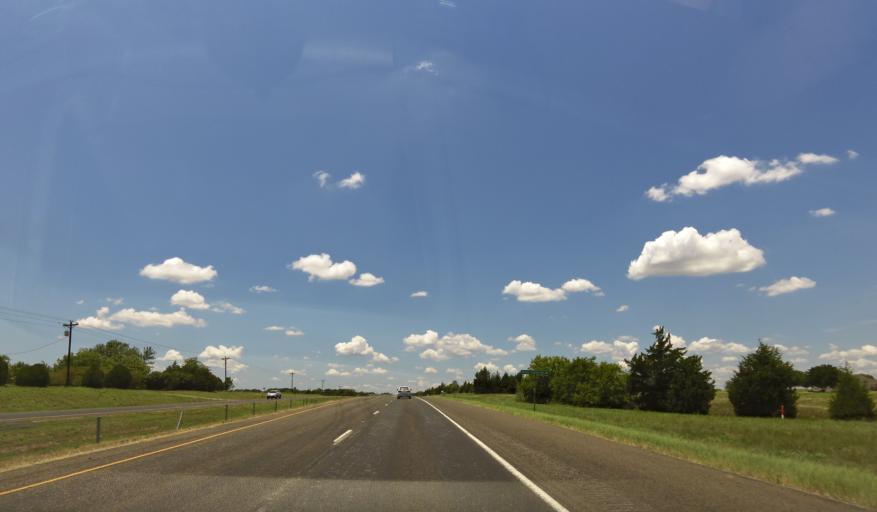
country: US
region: Texas
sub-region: Washington County
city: Brenham
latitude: 30.1912
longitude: -96.5338
